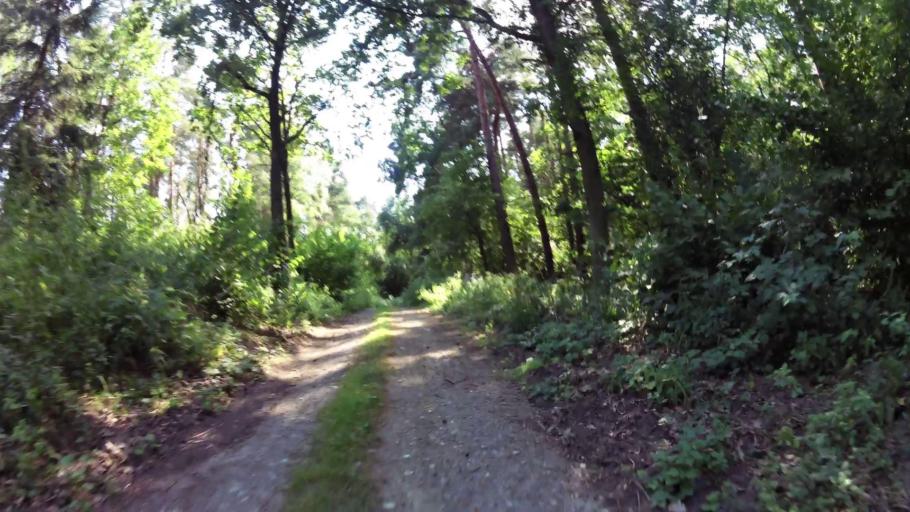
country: PL
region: West Pomeranian Voivodeship
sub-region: Powiat gryfinski
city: Moryn
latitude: 52.8824
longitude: 14.4327
